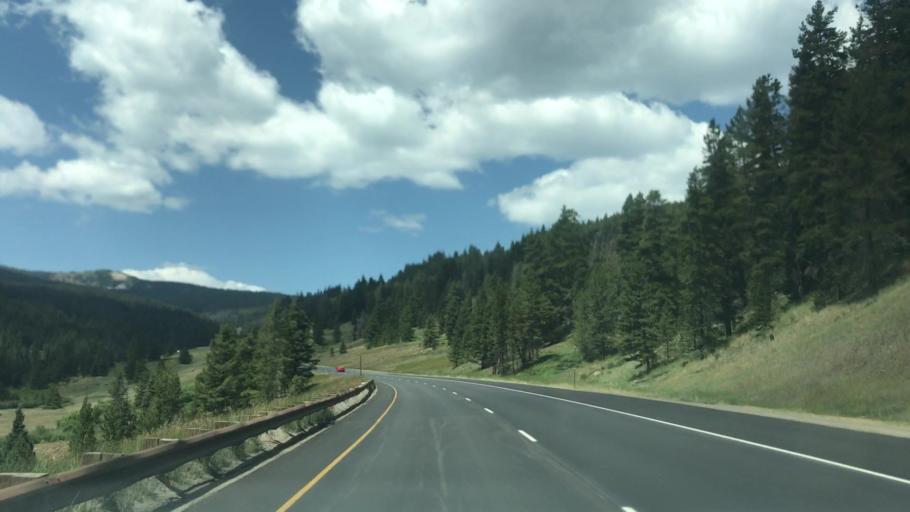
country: US
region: Colorado
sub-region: Summit County
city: Frisco
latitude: 39.5068
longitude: -106.1884
